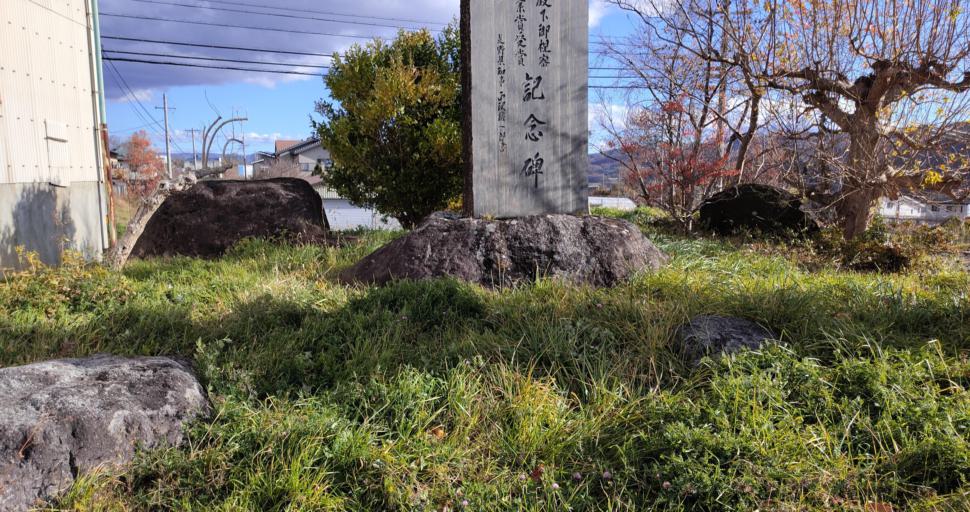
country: JP
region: Nagano
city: Komoro
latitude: 36.3491
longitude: 138.3780
